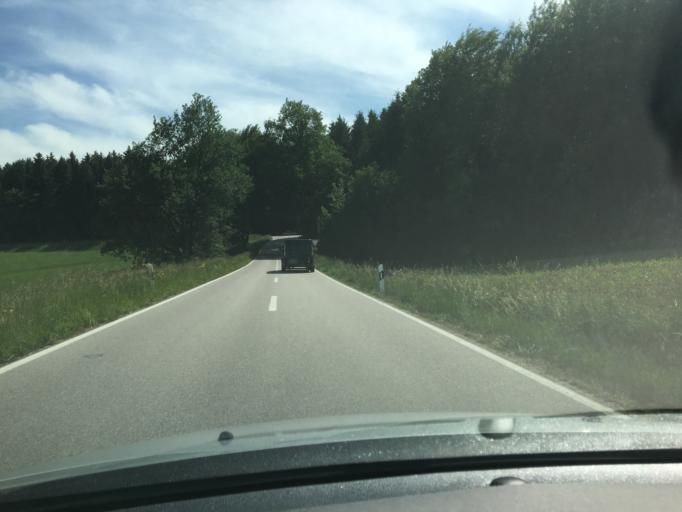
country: DE
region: Bavaria
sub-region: Upper Bavaria
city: Niedertaufkirchen
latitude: 48.3489
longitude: 12.5711
